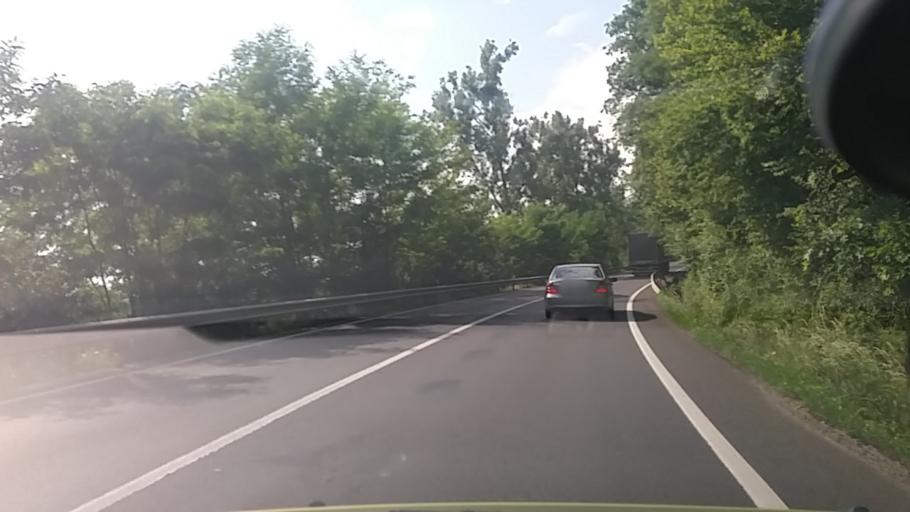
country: RO
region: Arad
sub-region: Comuna Varadia de Mures
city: Varadia de Mures
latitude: 46.0262
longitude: 22.1234
